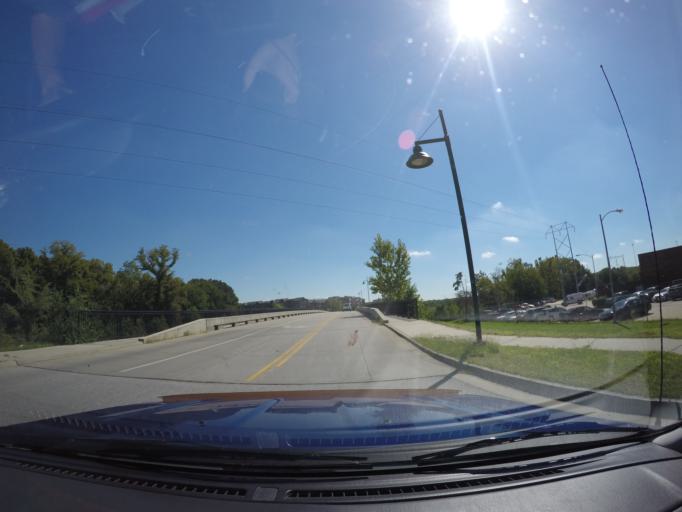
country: US
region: Kansas
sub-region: Johnson County
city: Leawood
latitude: 38.9359
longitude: -94.6352
